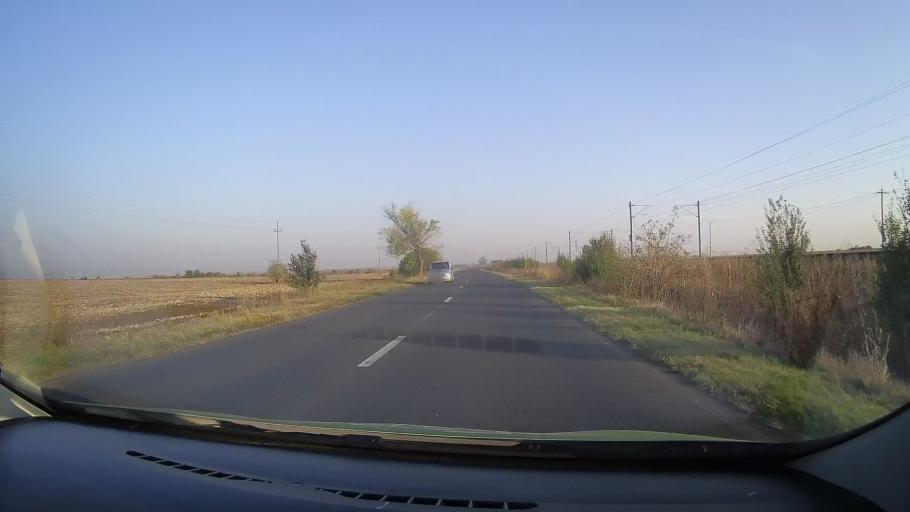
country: RO
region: Arad
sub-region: Comuna Sofronea
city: Sofronea
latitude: 46.2933
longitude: 21.3115
